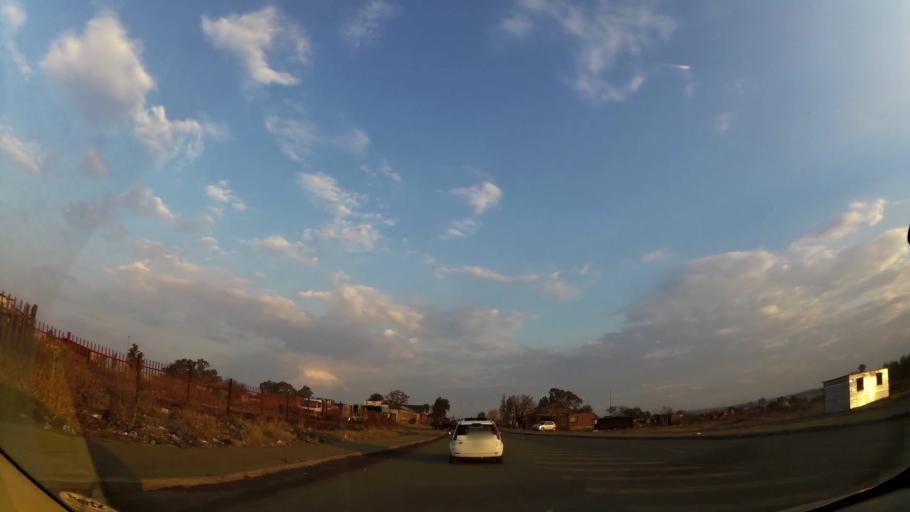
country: ZA
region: Gauteng
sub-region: City of Johannesburg Metropolitan Municipality
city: Orange Farm
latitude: -26.5389
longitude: 27.8842
